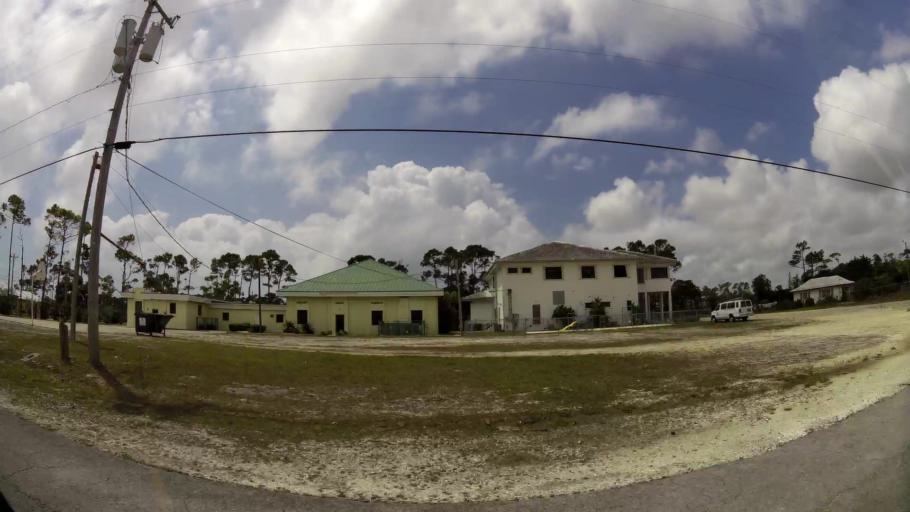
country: BS
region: Freeport
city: Lucaya
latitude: 26.5245
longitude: -78.6527
